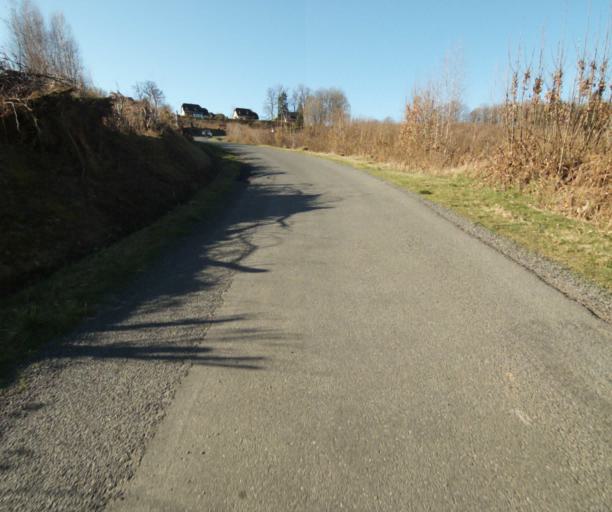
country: FR
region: Limousin
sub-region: Departement de la Correze
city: Seilhac
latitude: 45.3752
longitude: 1.7494
